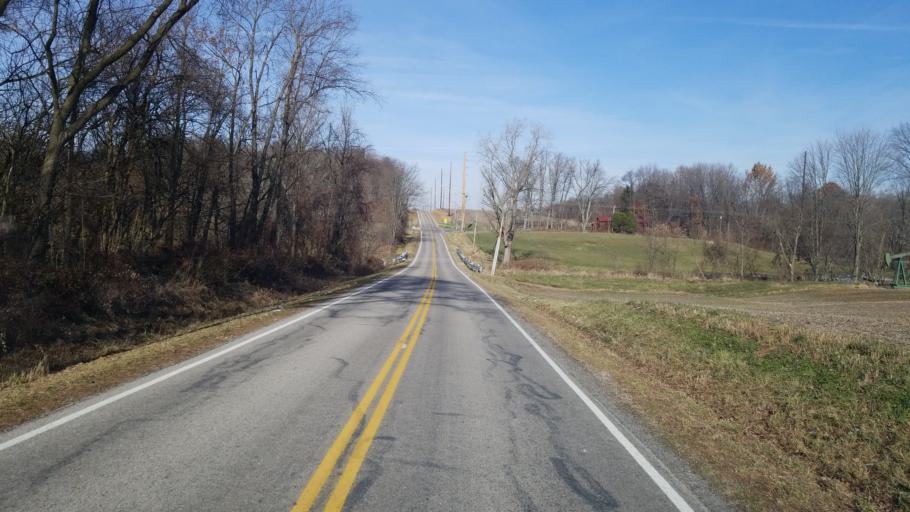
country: US
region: Ohio
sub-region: Huron County
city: Willard
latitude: 41.1173
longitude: -82.6860
